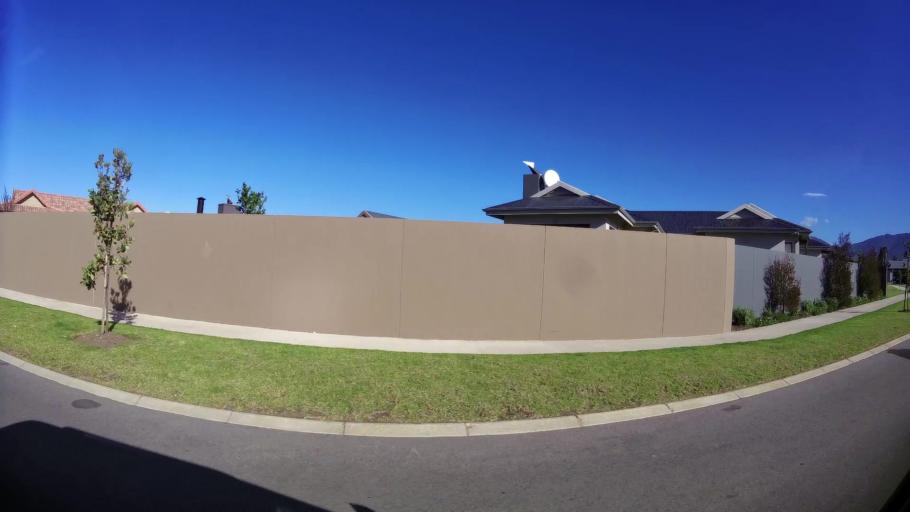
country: ZA
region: Western Cape
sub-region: Eden District Municipality
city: George
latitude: -33.9605
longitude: 22.4234
